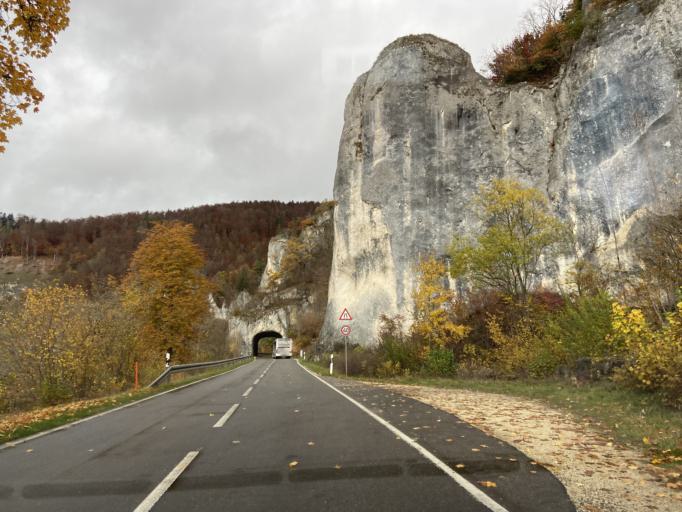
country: DE
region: Baden-Wuerttemberg
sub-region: Tuebingen Region
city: Stetten am Kalten Markt
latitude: 48.0915
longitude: 9.1084
